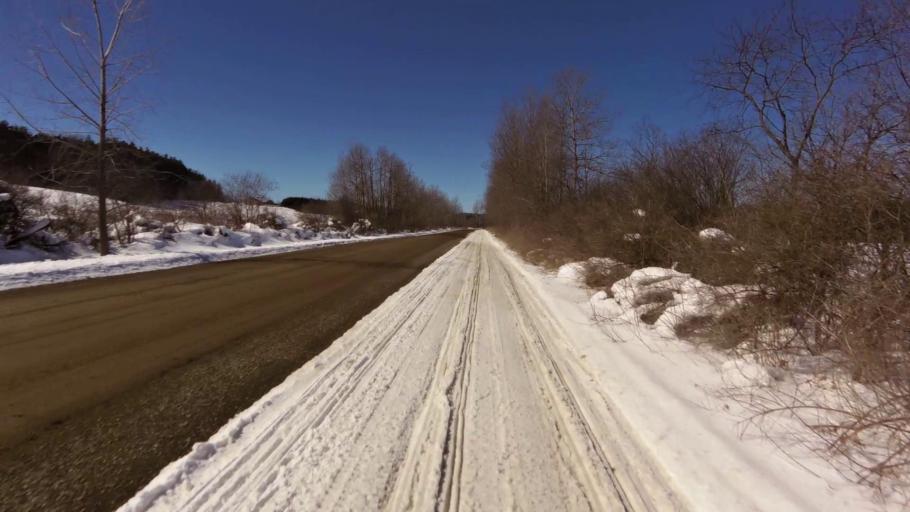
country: US
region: New York
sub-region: Cattaraugus County
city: Delevan
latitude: 42.4340
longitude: -78.4038
